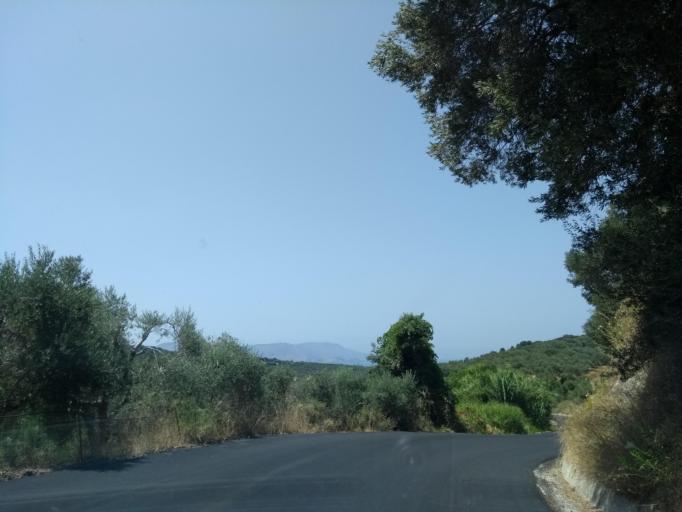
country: GR
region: Crete
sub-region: Nomos Chanias
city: Georgioupolis
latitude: 35.3259
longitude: 24.2999
